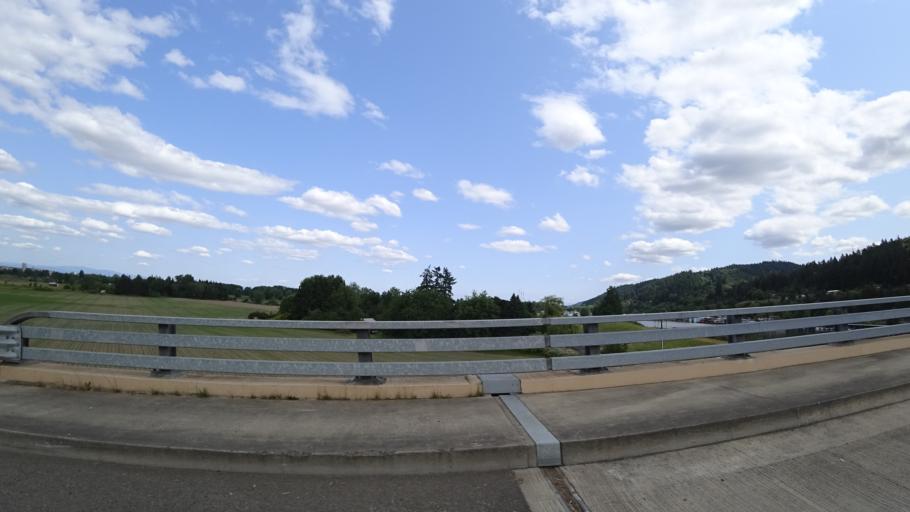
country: US
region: Oregon
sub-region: Washington County
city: Bethany
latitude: 45.6287
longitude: -122.8148
